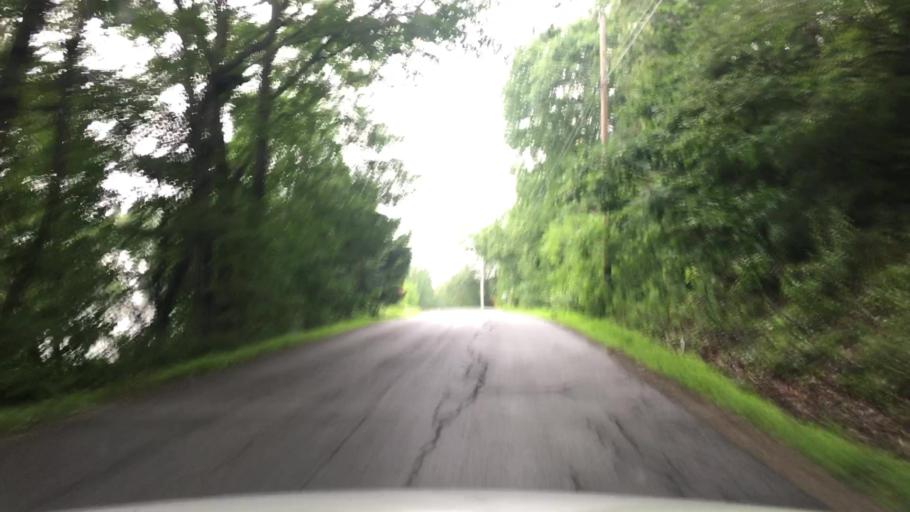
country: US
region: Maine
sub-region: Knox County
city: Hope
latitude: 44.2164
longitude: -69.1821
